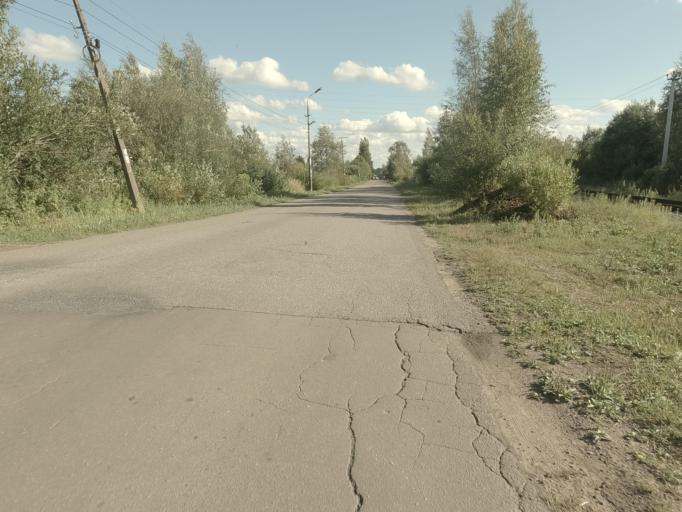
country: RU
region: Leningrad
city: Imeni Morozova
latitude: 59.9659
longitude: 31.0289
